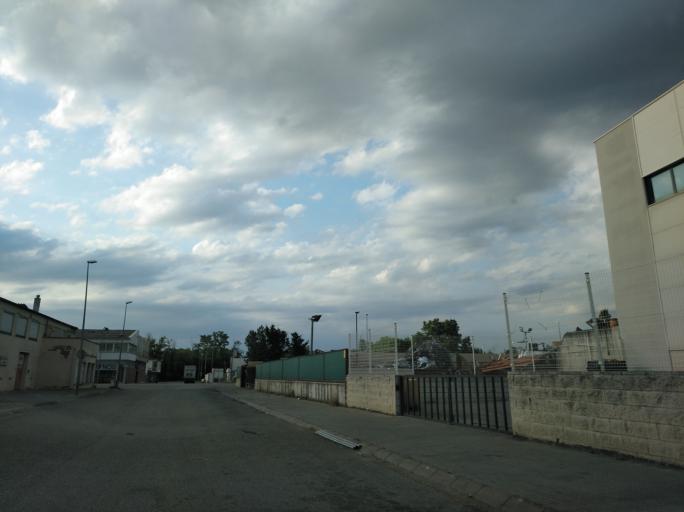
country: ES
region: Catalonia
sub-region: Provincia de Girona
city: Vilablareix
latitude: 41.9692
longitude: 2.7762
